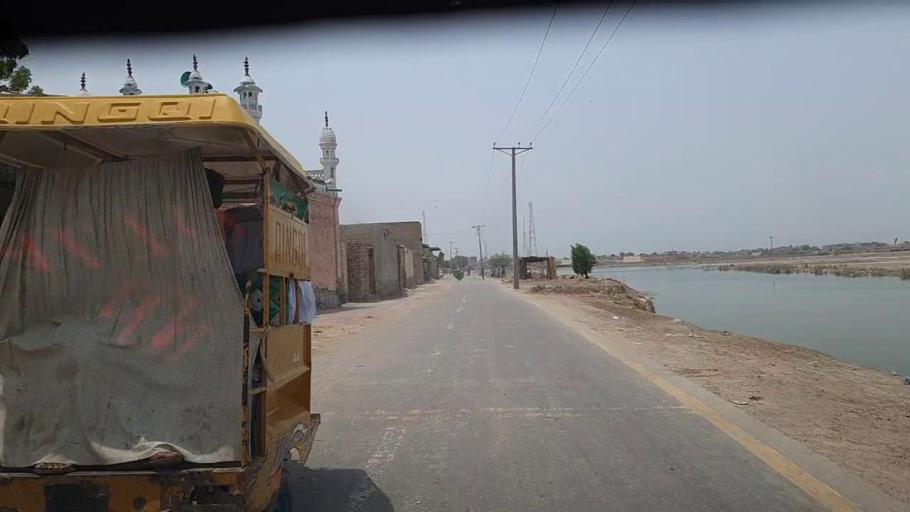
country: PK
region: Sindh
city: Sita Road
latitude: 27.0417
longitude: 67.8565
